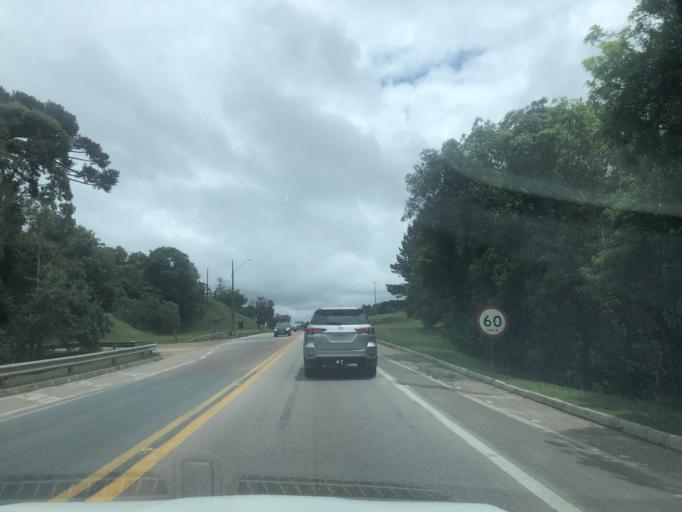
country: BR
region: Parana
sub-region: Araucaria
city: Araucaria
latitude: -25.8119
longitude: -49.3279
